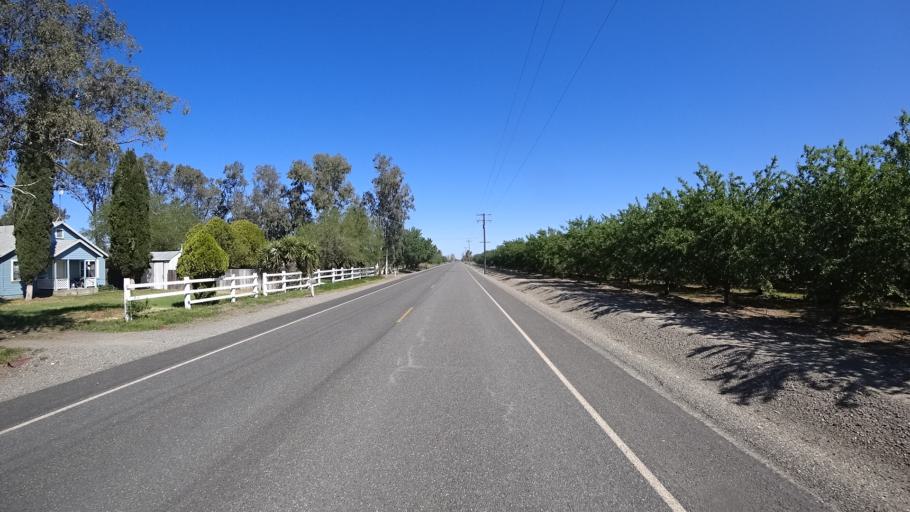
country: US
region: California
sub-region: Glenn County
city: Hamilton City
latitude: 39.7157
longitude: -122.1043
